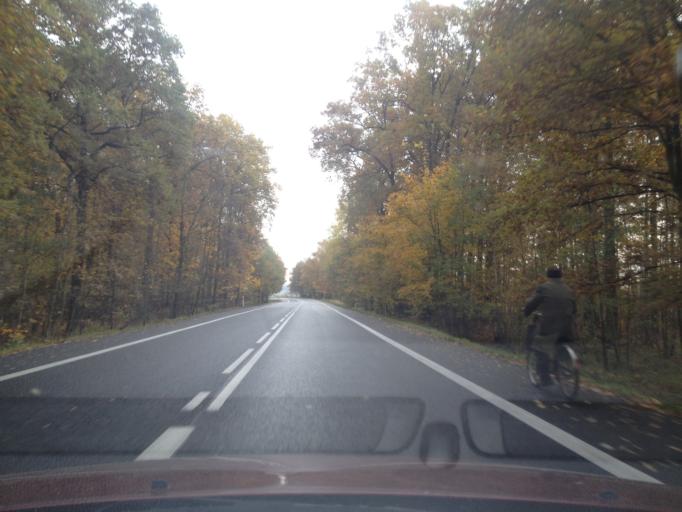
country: PL
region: Lower Silesian Voivodeship
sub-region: Powiat zgorzelecki
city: Lagow
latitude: 51.1530
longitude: 15.0779
